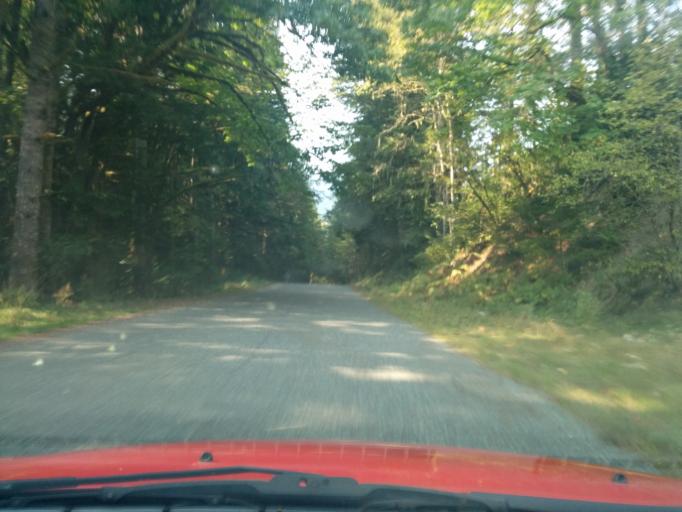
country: US
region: Washington
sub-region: Snohomish County
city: Darrington
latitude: 48.5290
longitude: -121.3924
